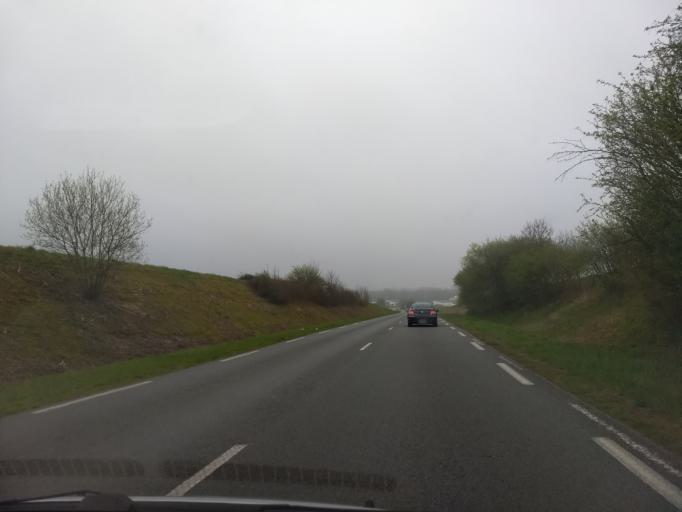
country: FR
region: Nord-Pas-de-Calais
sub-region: Departement du Pas-de-Calais
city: Verton
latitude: 50.4119
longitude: 1.6599
